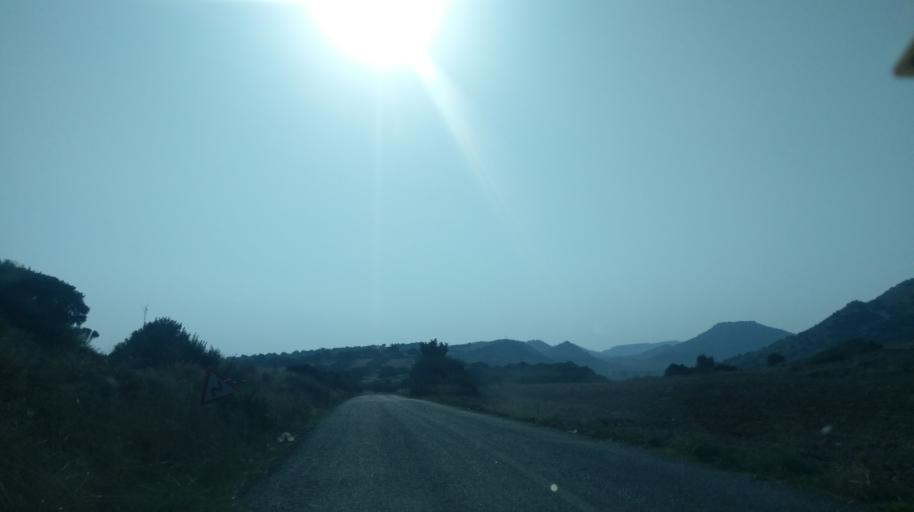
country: CY
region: Ammochostos
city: Rizokarpaso
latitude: 35.5211
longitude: 34.3187
